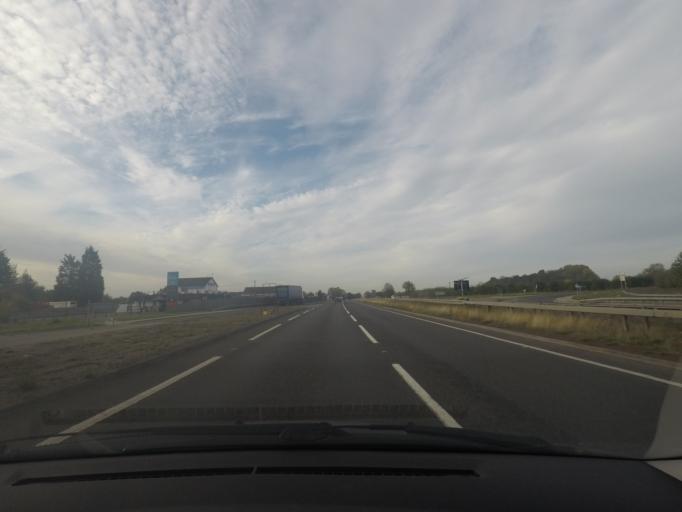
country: GB
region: England
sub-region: City of York
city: Askham Richard
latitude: 53.9076
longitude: -1.1851
